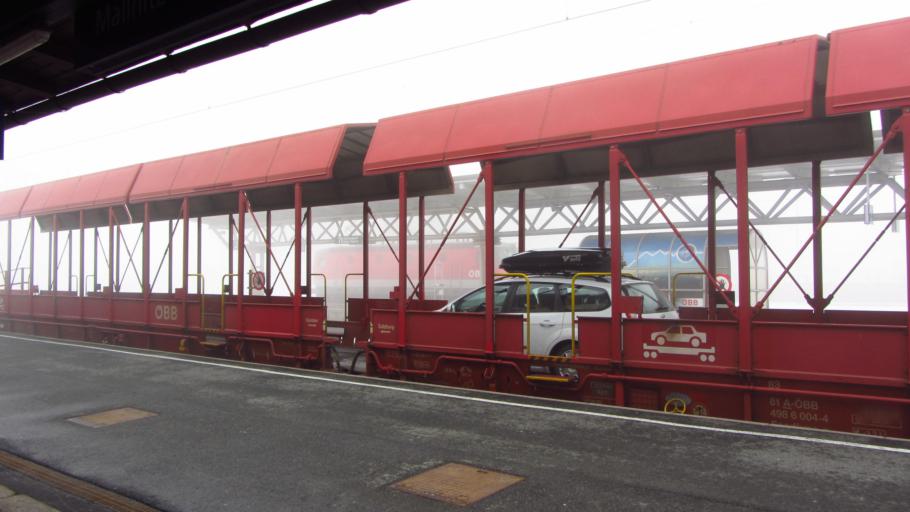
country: AT
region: Carinthia
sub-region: Politischer Bezirk Spittal an der Drau
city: Obervellach
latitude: 46.9803
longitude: 13.1767
